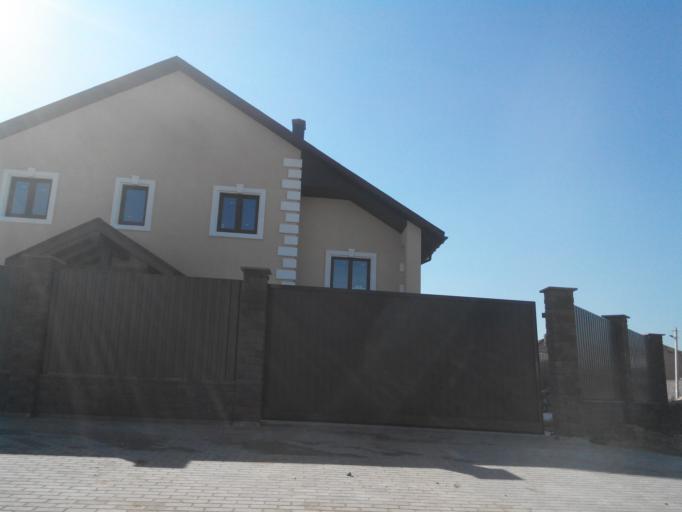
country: BY
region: Minsk
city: Zhdanovichy
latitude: 53.9234
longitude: 27.4092
